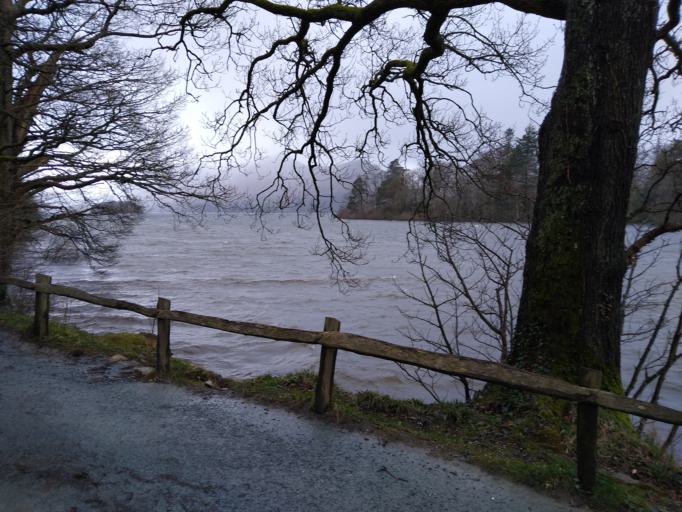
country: GB
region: England
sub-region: Cumbria
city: Keswick
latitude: 54.5923
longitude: -3.1407
